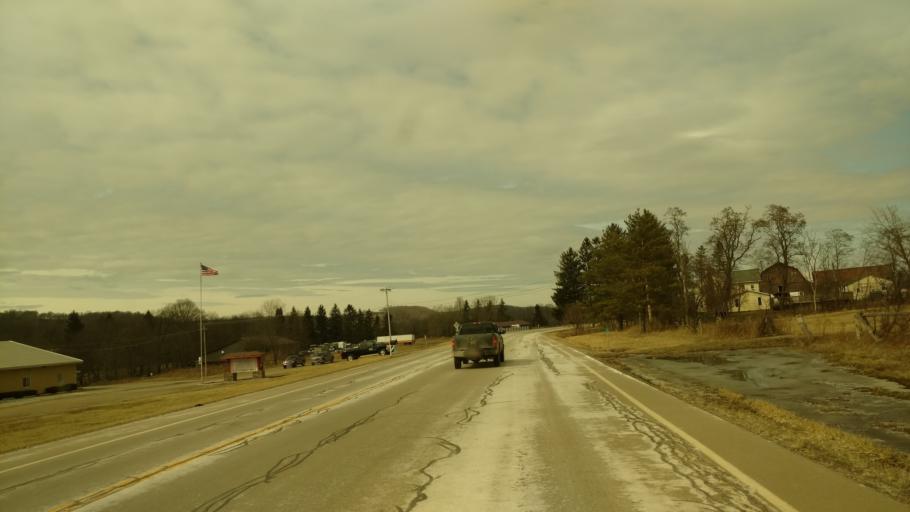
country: US
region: New York
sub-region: Allegany County
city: Wellsville
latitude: 42.0609
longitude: -77.9181
